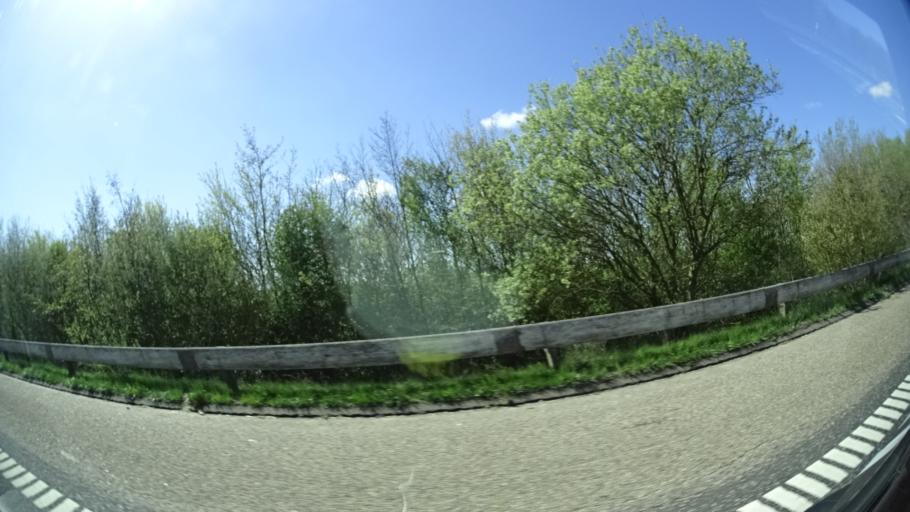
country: DK
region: Central Jutland
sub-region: Favrskov Kommune
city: Hadsten
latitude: 56.3522
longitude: 10.1169
